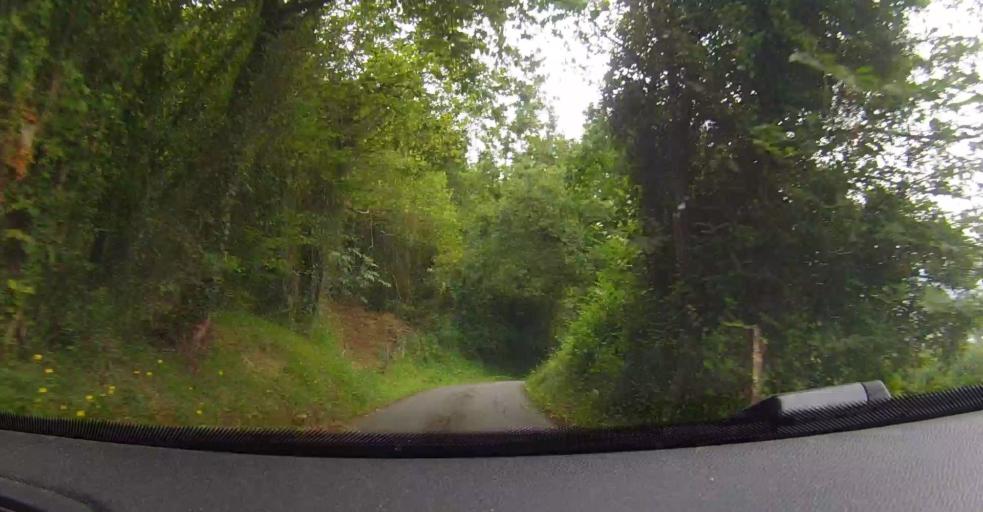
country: ES
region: Basque Country
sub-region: Bizkaia
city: Sopuerta
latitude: 43.2594
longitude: -3.1382
